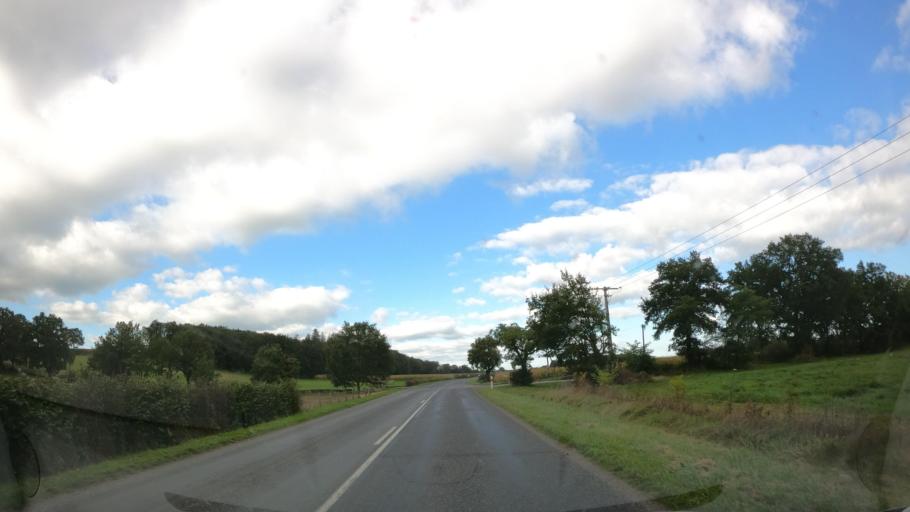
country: FR
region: Auvergne
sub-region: Departement de l'Allier
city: Dompierre-sur-Besbre
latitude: 46.4818
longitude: 3.6522
